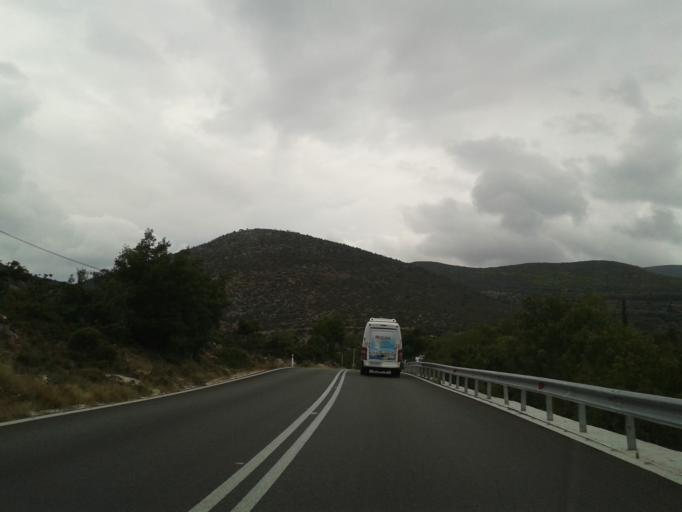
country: GR
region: Peloponnese
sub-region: Nomos Korinthias
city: Ayios Vasilios
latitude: 37.7898
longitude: 22.7278
